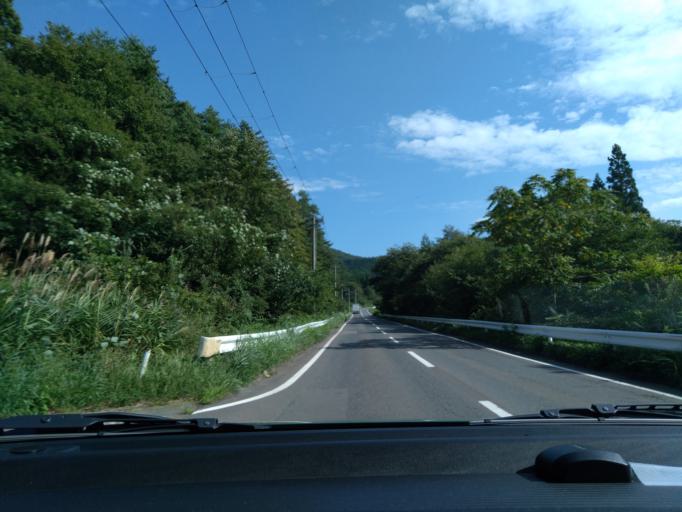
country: JP
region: Iwate
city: Shizukuishi
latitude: 39.6432
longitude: 141.0021
